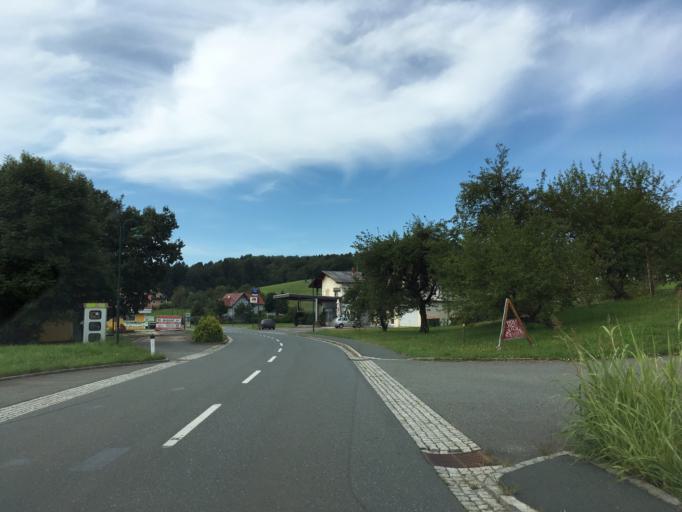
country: AT
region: Styria
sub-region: Politischer Bezirk Leibnitz
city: Pistorf
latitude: 46.7928
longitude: 15.3754
